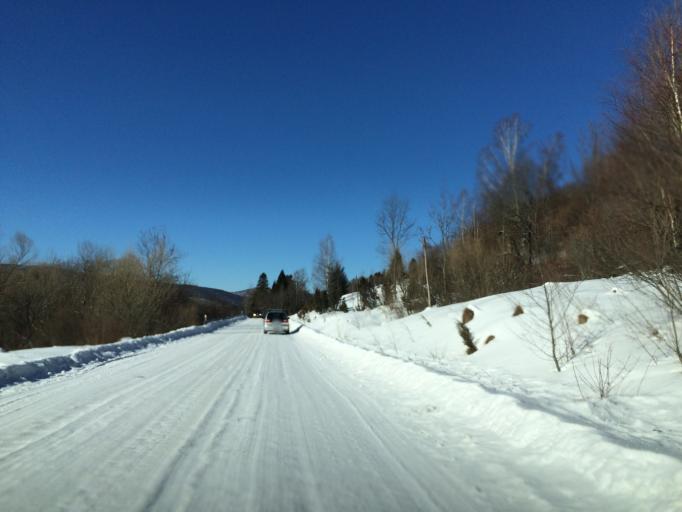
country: PL
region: Subcarpathian Voivodeship
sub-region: Powiat leski
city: Cisna
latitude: 49.1461
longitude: 22.5146
